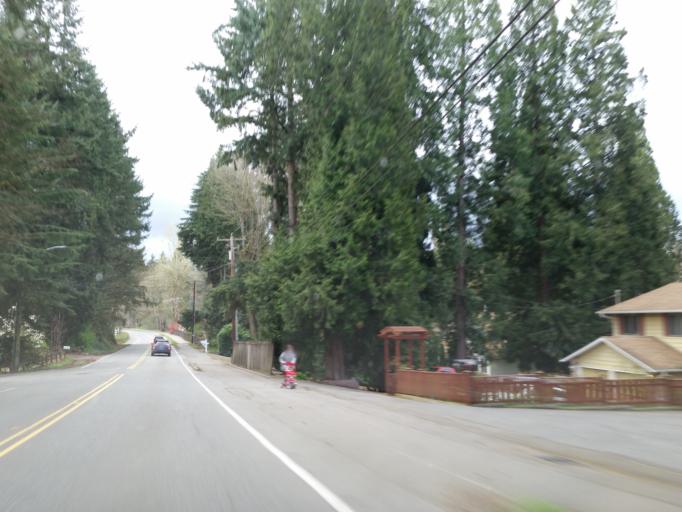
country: US
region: Washington
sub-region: King County
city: Woodinville
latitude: 47.7631
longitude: -122.1636
